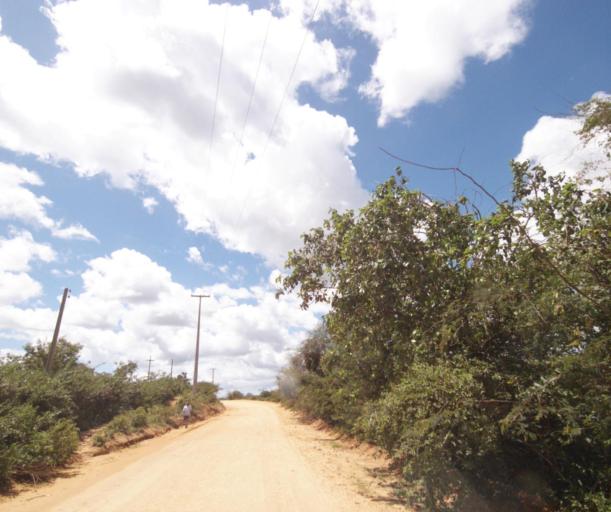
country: BR
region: Bahia
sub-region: Pocoes
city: Pocoes
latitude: -14.3546
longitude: -40.5884
